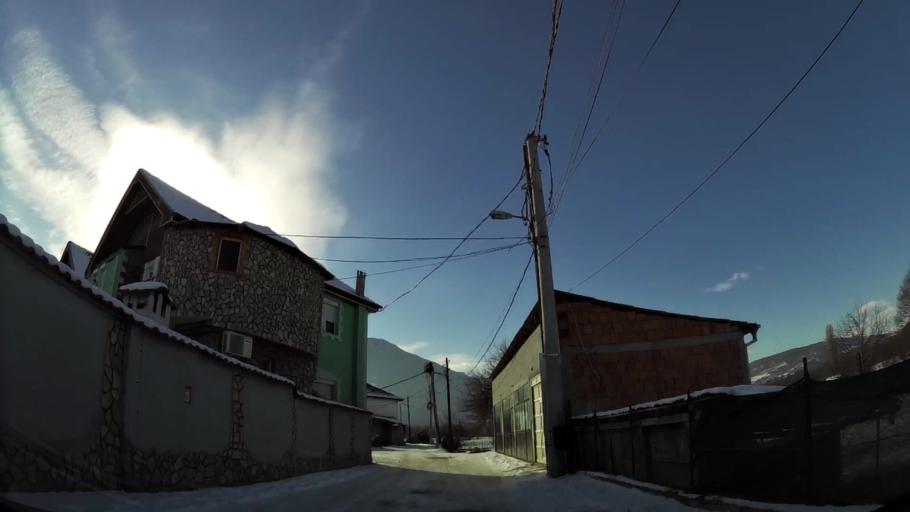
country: MK
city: Grchec
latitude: 41.9899
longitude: 21.3259
